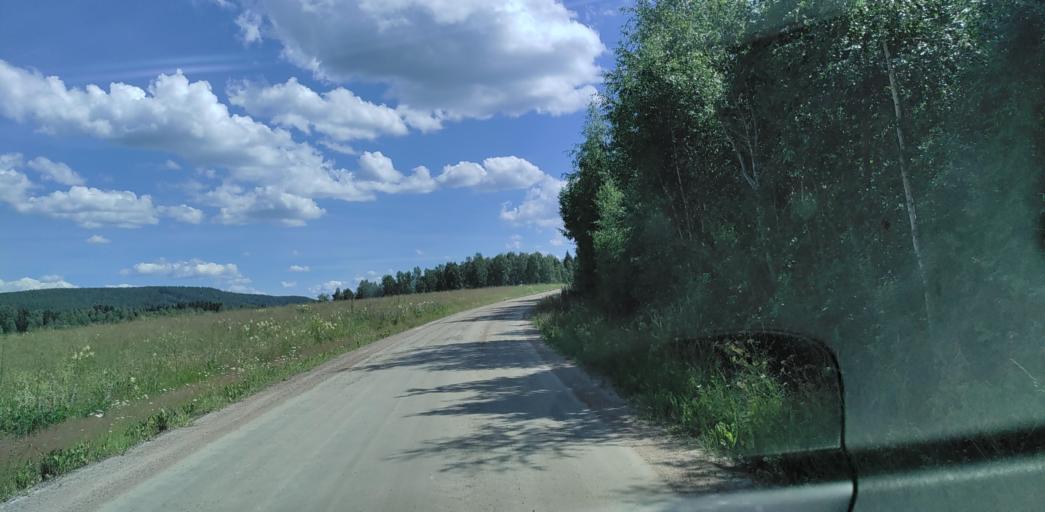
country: SE
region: Vaermland
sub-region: Hagfors Kommun
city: Ekshaerad
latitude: 60.1244
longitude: 13.4801
